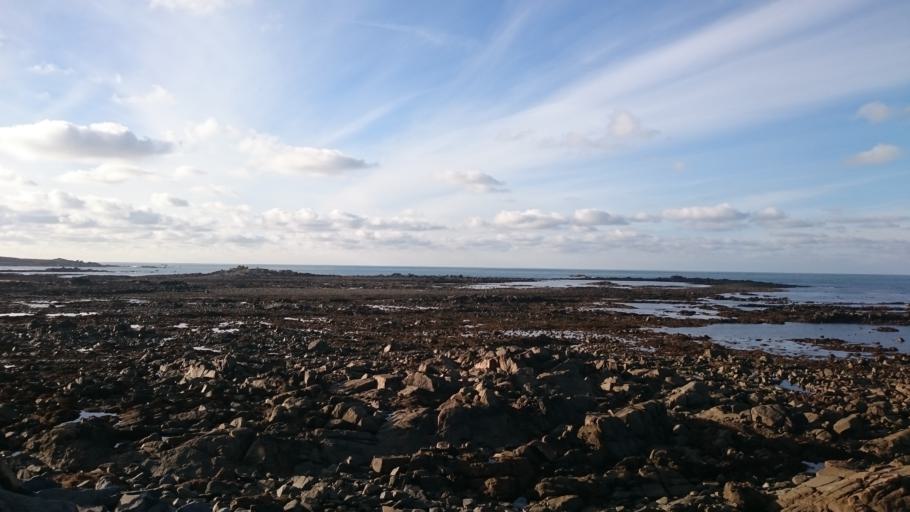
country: GG
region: St Peter Port
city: Saint Peter Port
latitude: 49.4609
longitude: -2.6423
